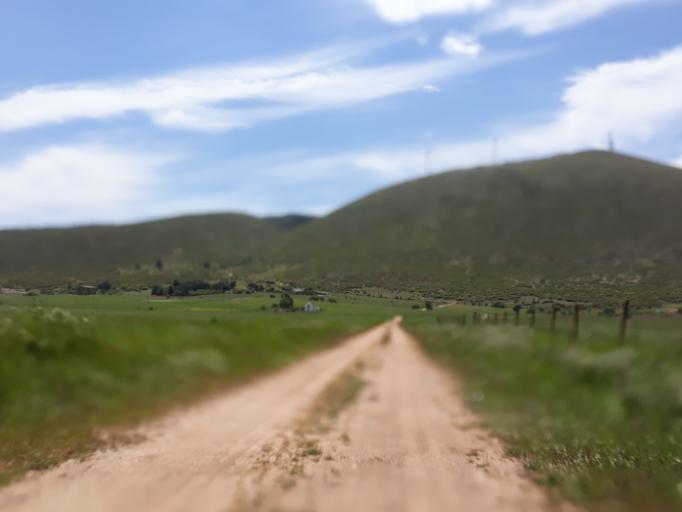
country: GR
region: Central Greece
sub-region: Nomos Voiotias
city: Ayios Thomas
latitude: 38.1859
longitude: 23.5614
